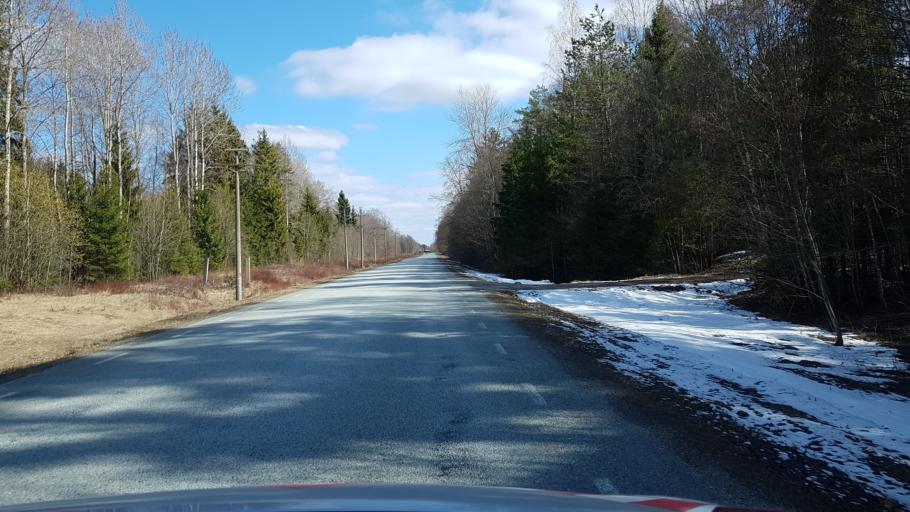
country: EE
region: Laeaene-Virumaa
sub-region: Tapa vald
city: Tapa
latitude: 59.2541
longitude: 25.7217
